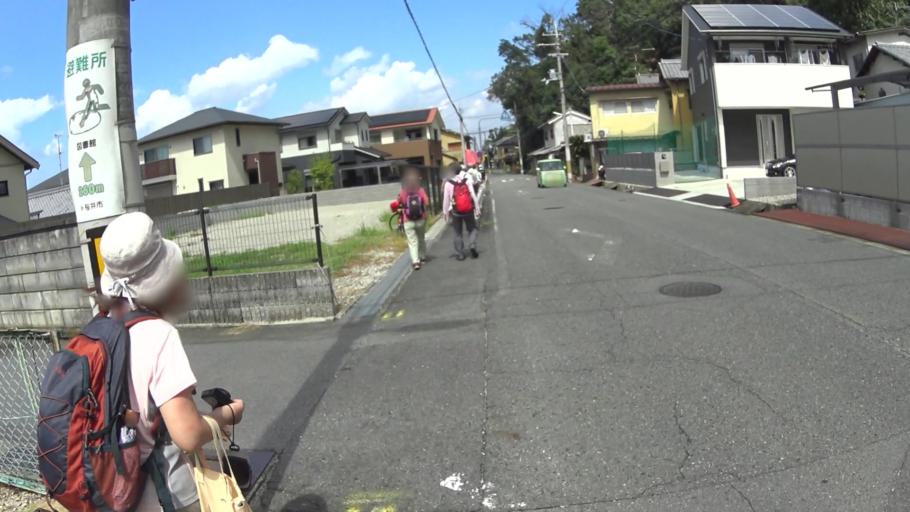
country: JP
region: Nara
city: Sakurai
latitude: 34.5044
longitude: 135.8527
